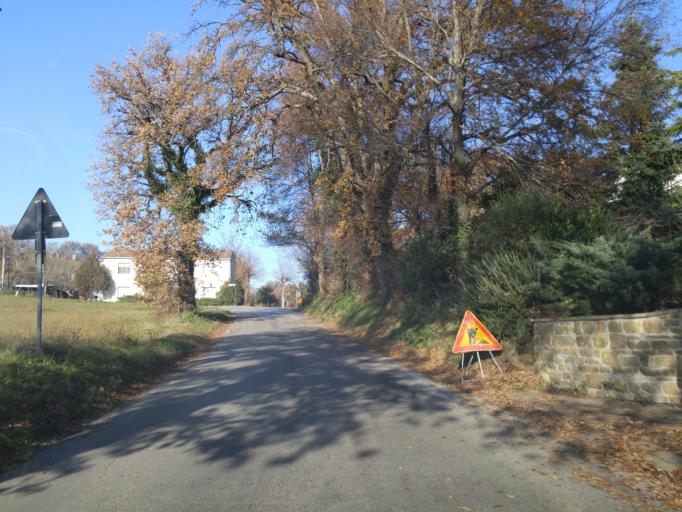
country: IT
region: The Marches
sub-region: Provincia di Pesaro e Urbino
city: Montefelcino
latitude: 43.7273
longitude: 12.8449
